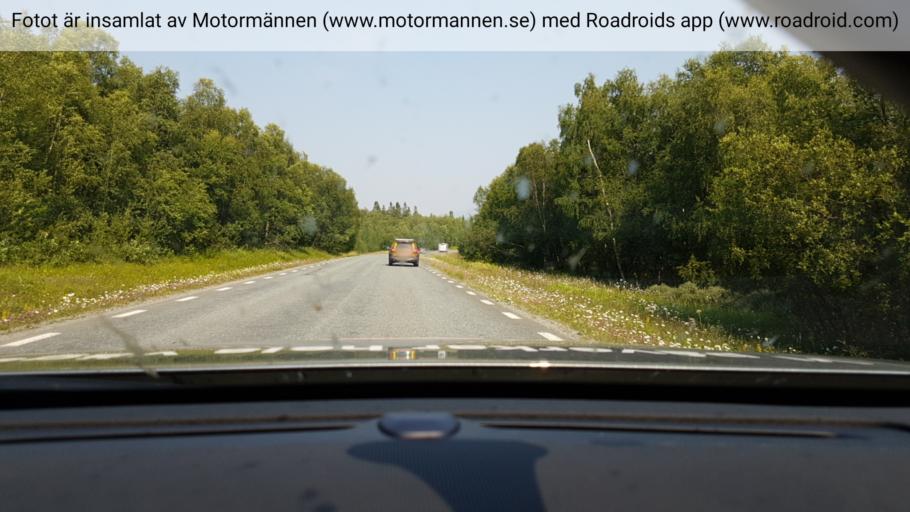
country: NO
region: Nordland
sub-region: Rana
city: Mo i Rana
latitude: 65.7676
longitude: 15.1132
